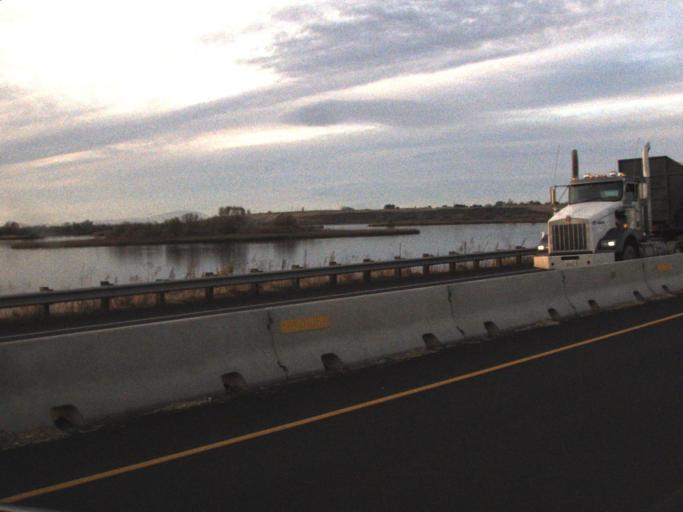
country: US
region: Washington
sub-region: Walla Walla County
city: Burbank
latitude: 46.1557
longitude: -118.9410
